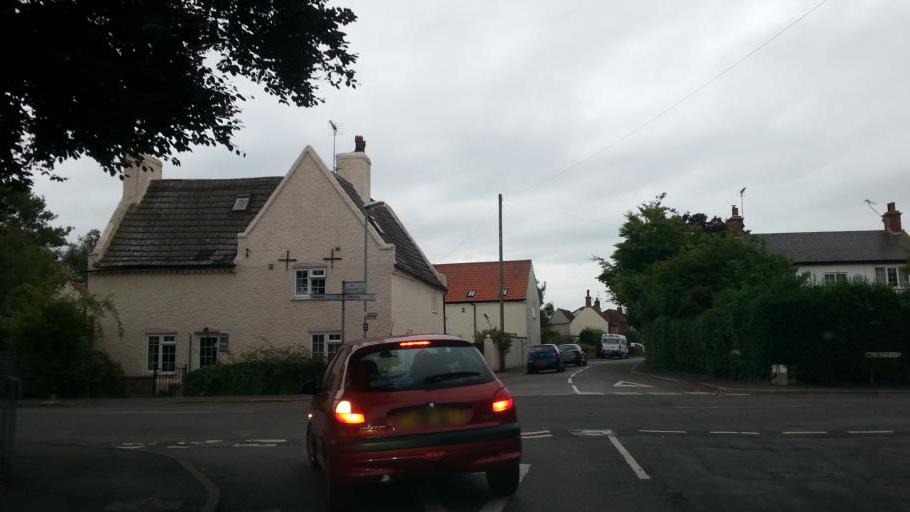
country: GB
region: England
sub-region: Lincolnshire
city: Long Bennington
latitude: 53.0314
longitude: -0.7341
